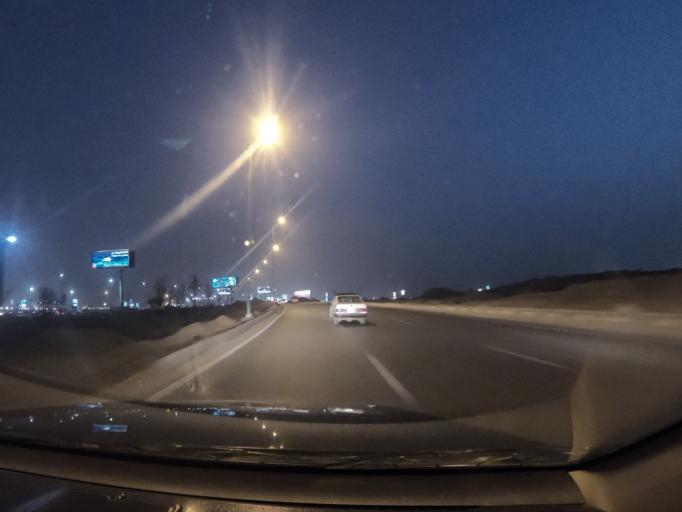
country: EG
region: Muhafazat al Qahirah
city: Cairo
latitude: 30.0228
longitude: 31.4008
